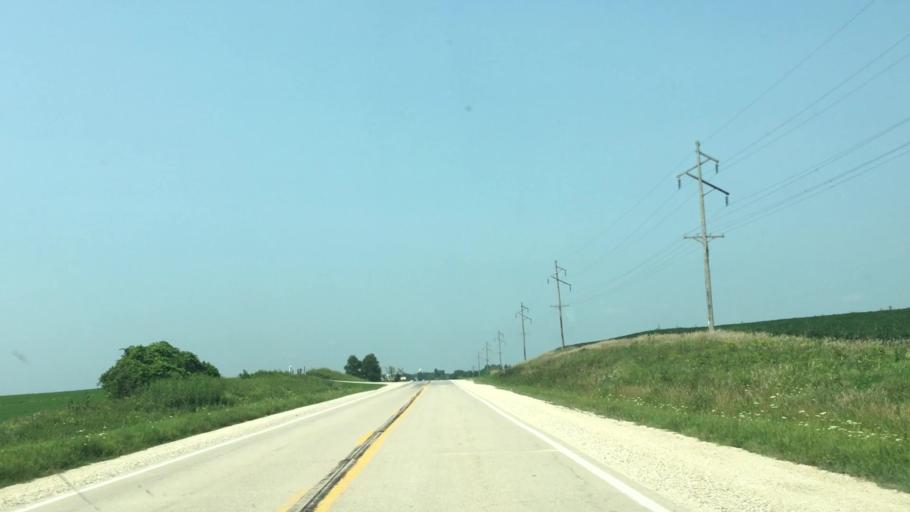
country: US
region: Iowa
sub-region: Winneshiek County
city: Decorah
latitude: 43.1478
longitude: -91.8643
